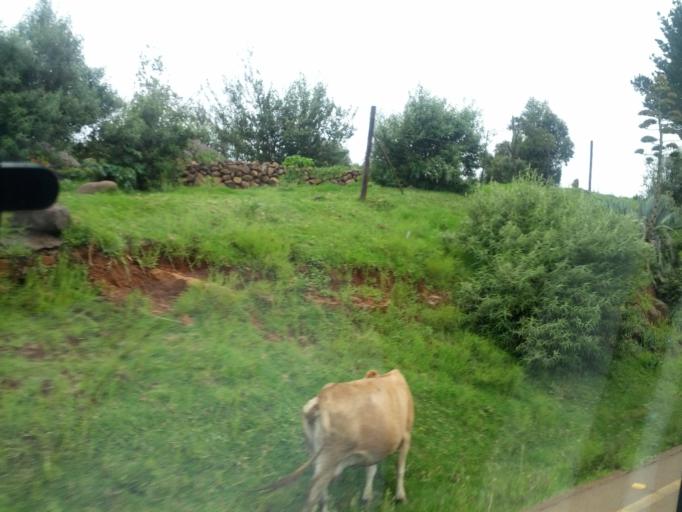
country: LS
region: Butha-Buthe
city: Butha-Buthe
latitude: -29.0328
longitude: 28.2685
